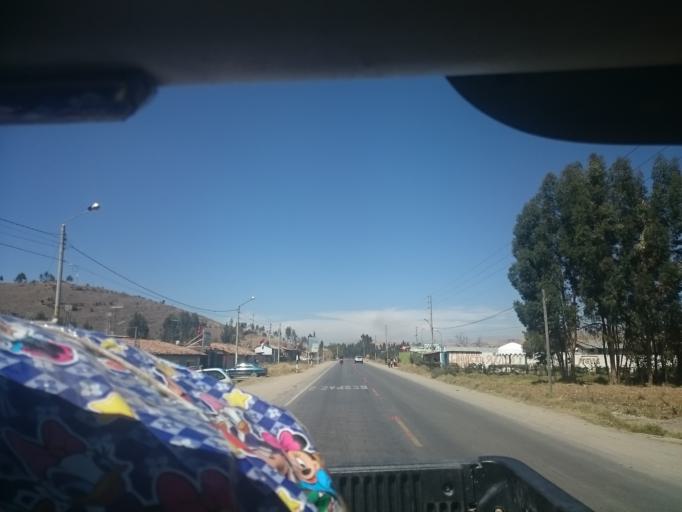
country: PE
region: Junin
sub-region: Provincia de Jauja
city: San Lorenzo
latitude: -11.8664
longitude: -75.3725
